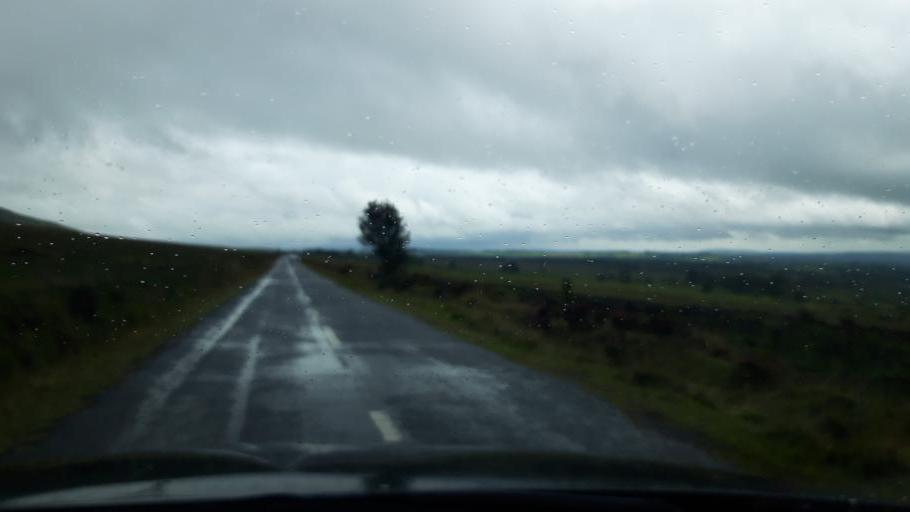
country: IE
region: Munster
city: Cahir
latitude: 52.2141
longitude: -7.9296
